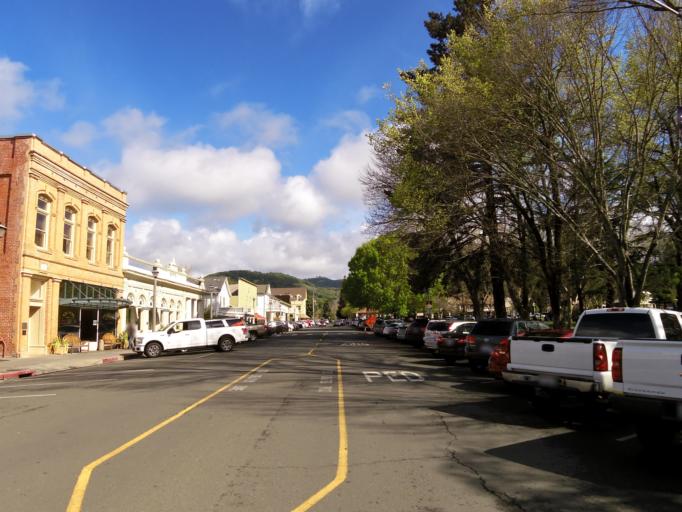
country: US
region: California
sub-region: Sonoma County
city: Sonoma
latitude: 38.2924
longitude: -122.4589
